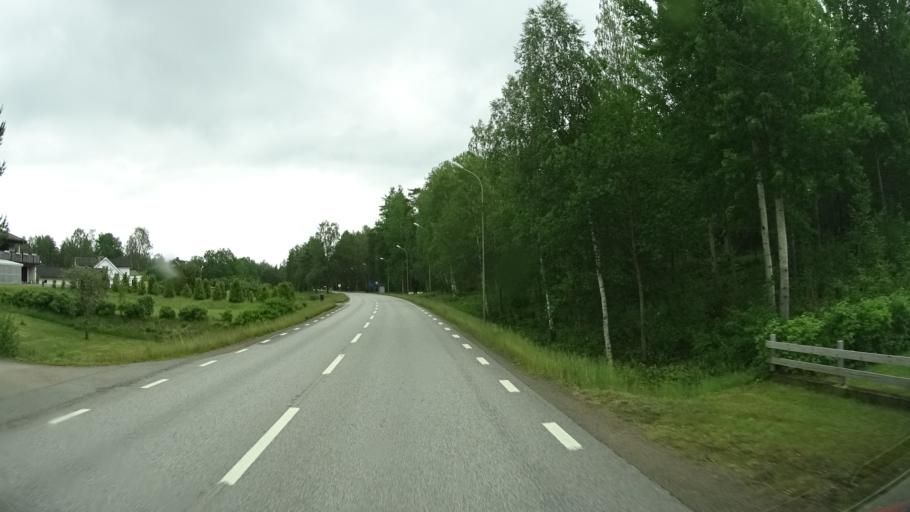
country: SE
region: Kalmar
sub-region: Hultsfreds Kommun
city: Hultsfred
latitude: 57.5355
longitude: 15.7629
